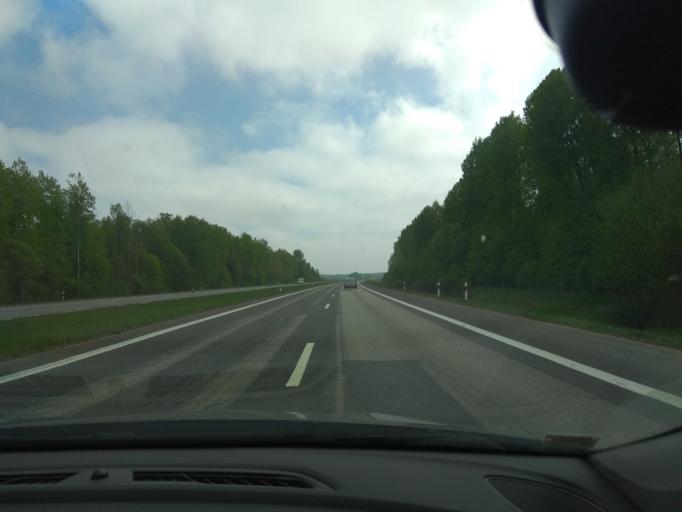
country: LT
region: Vilnius County
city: Ukmerge
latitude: 55.4607
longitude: 24.6639
